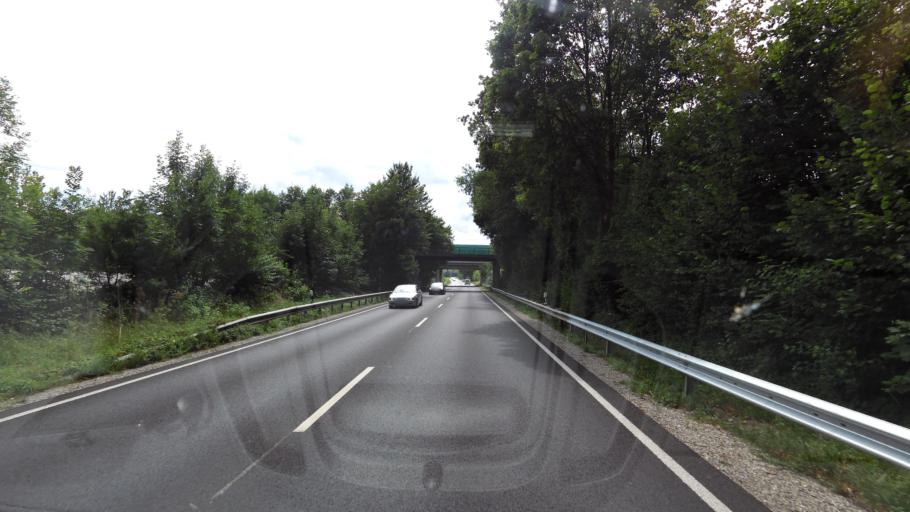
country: DE
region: Bavaria
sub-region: Upper Bavaria
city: Freilassing
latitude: 47.8356
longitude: 12.9848
